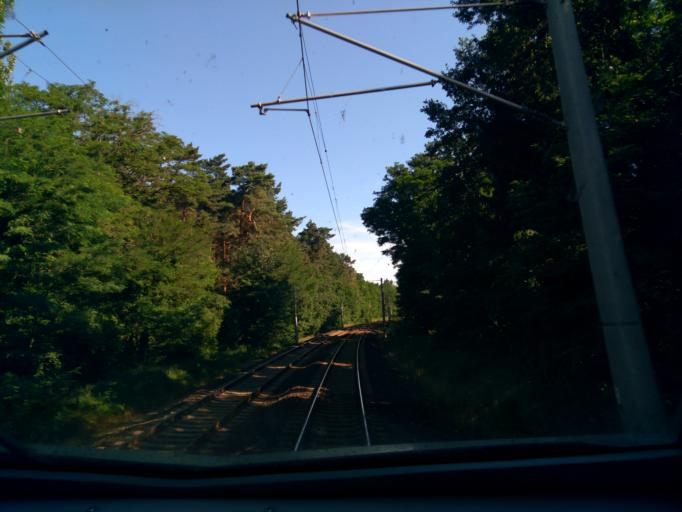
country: DE
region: Brandenburg
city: Bestensee
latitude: 52.2497
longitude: 13.6329
